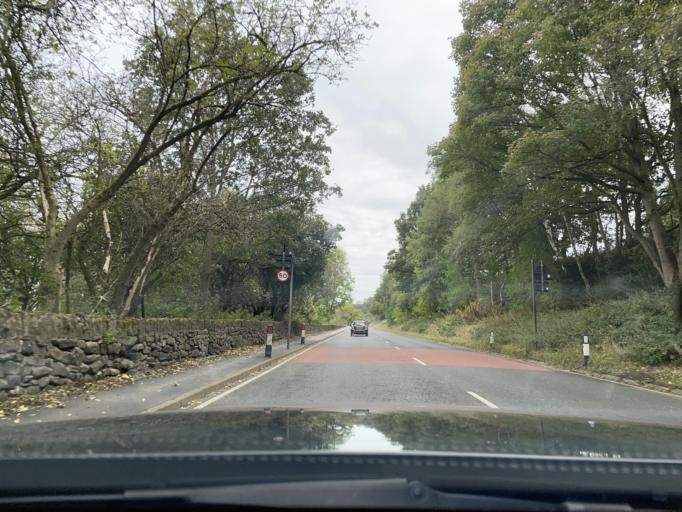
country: GB
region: England
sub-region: Sheffield
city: Oughtibridge
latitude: 53.3801
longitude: -1.5547
